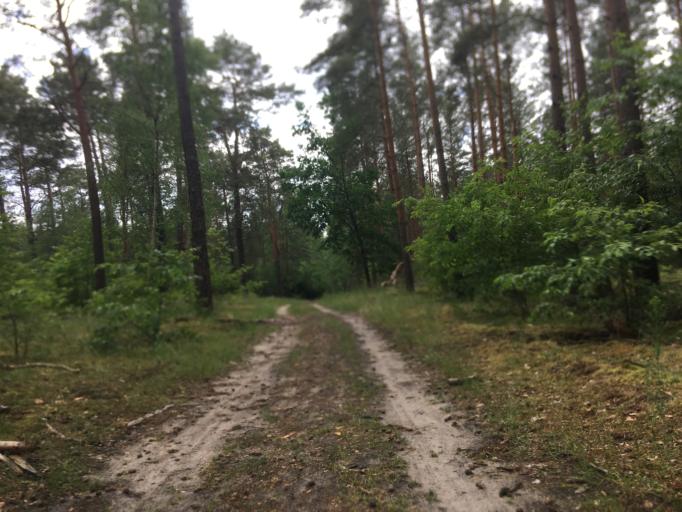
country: DE
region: Berlin
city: Rahnsdorf
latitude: 52.4196
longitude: 13.7010
